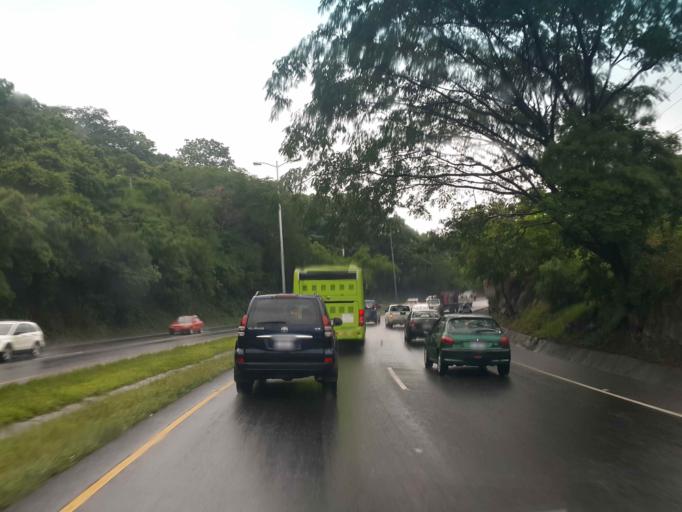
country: CR
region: San Jose
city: Santa Ana
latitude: 9.9480
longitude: -84.1749
